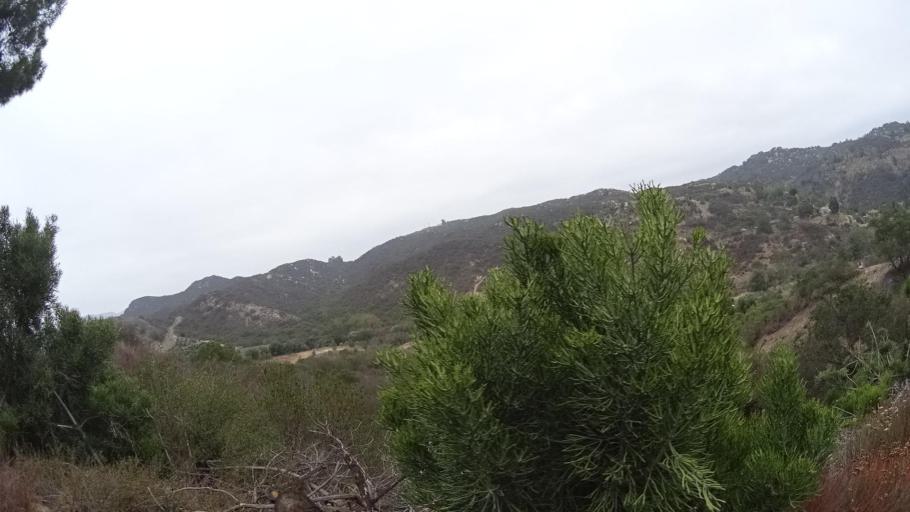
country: US
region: California
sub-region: San Diego County
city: Fallbrook
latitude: 33.4454
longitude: -117.2878
